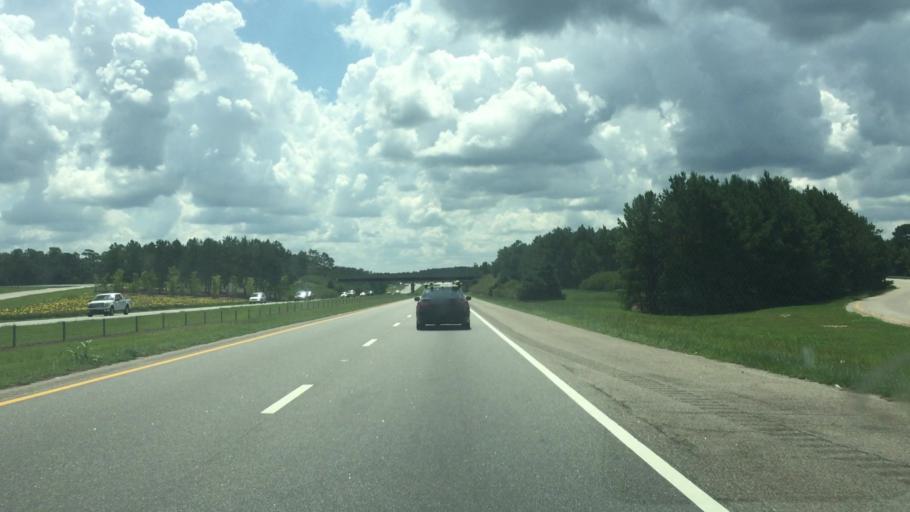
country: US
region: North Carolina
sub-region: Richmond County
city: Hamlet
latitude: 34.8608
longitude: -79.7459
